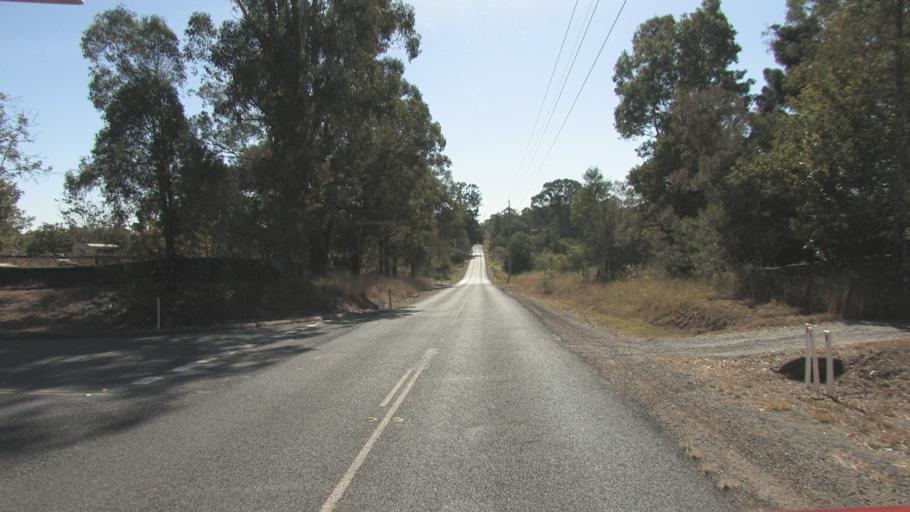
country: AU
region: Queensland
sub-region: Logan
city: Cedar Vale
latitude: -27.8750
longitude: 153.0168
